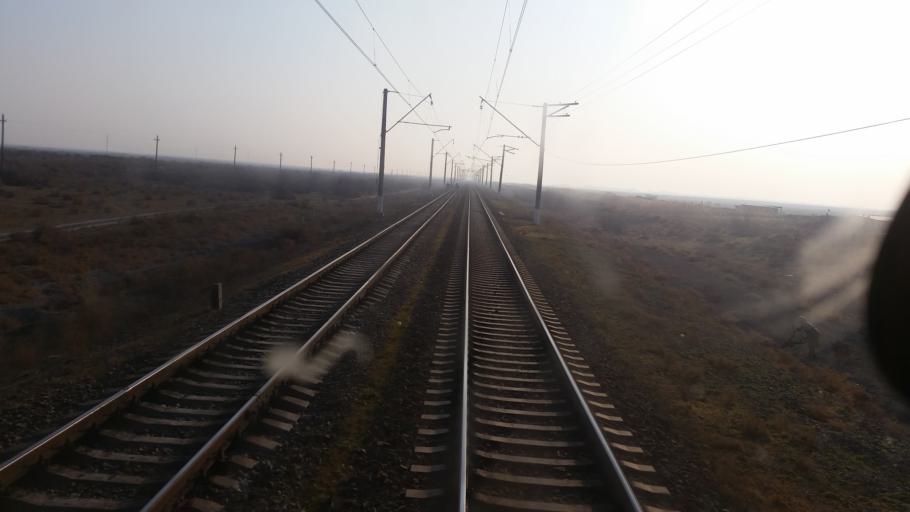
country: AZ
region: Yevlax City
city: Yevlakh
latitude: 40.5962
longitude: 47.2619
